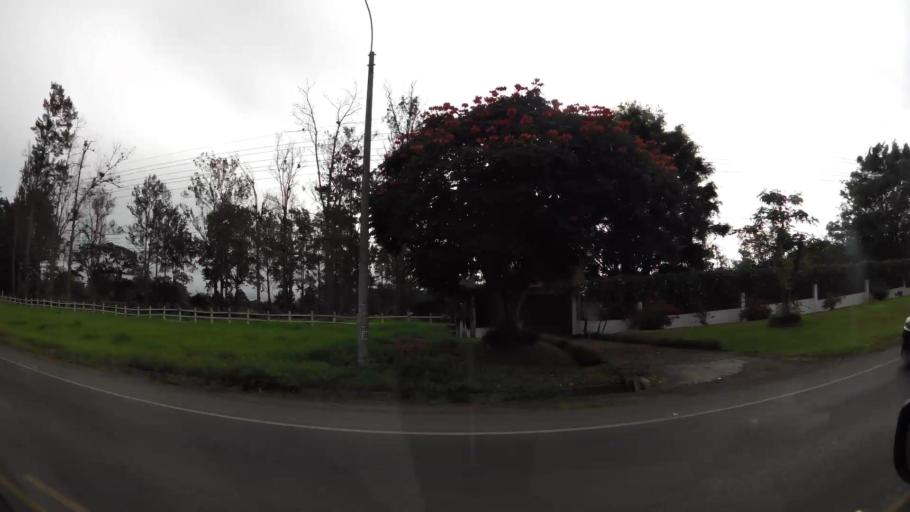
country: CR
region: Cartago
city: Cartago
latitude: 9.8626
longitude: -83.9463
